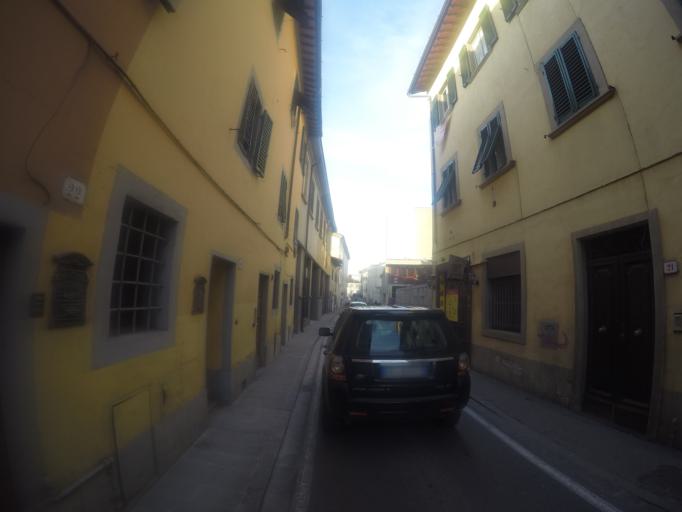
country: IT
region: Tuscany
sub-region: Provincia di Prato
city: Prato
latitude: 43.8792
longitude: 11.1024
